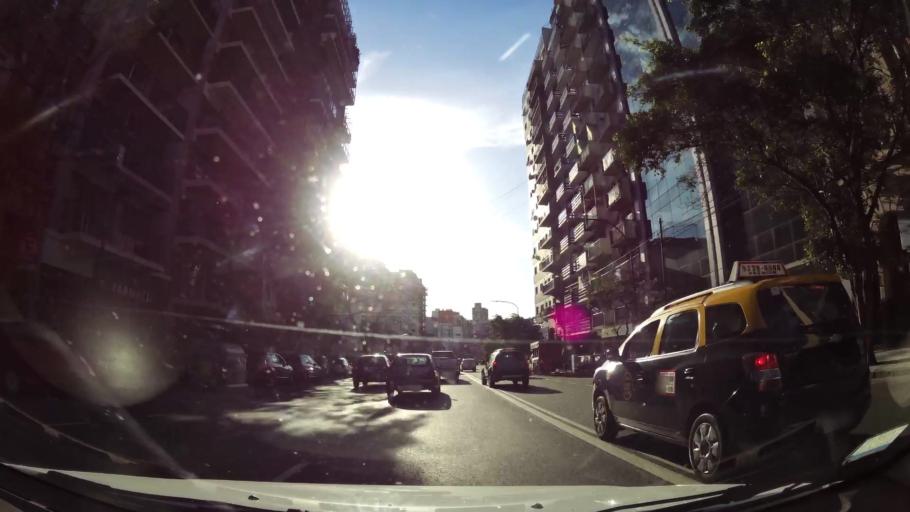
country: AR
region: Buenos Aires F.D.
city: Retiro
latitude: -34.5996
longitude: -58.3962
